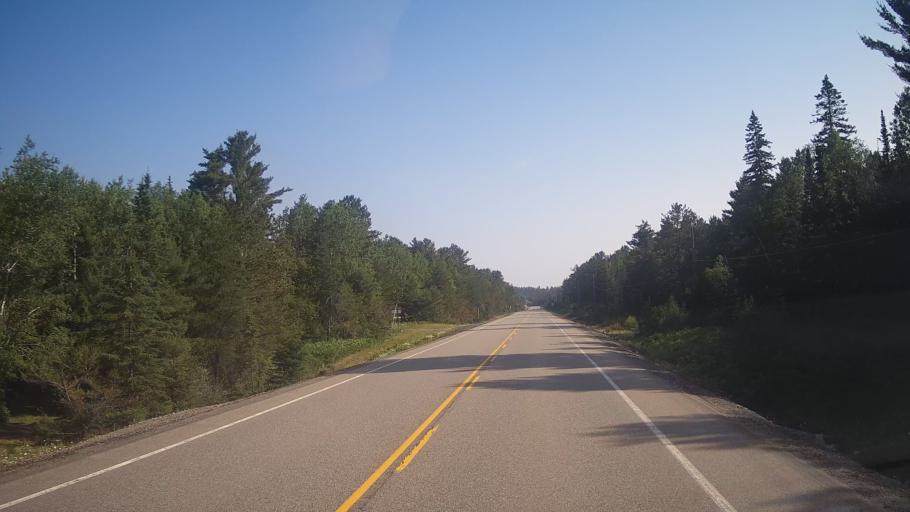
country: CA
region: Ontario
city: Rayside-Balfour
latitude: 46.7485
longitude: -81.6011
